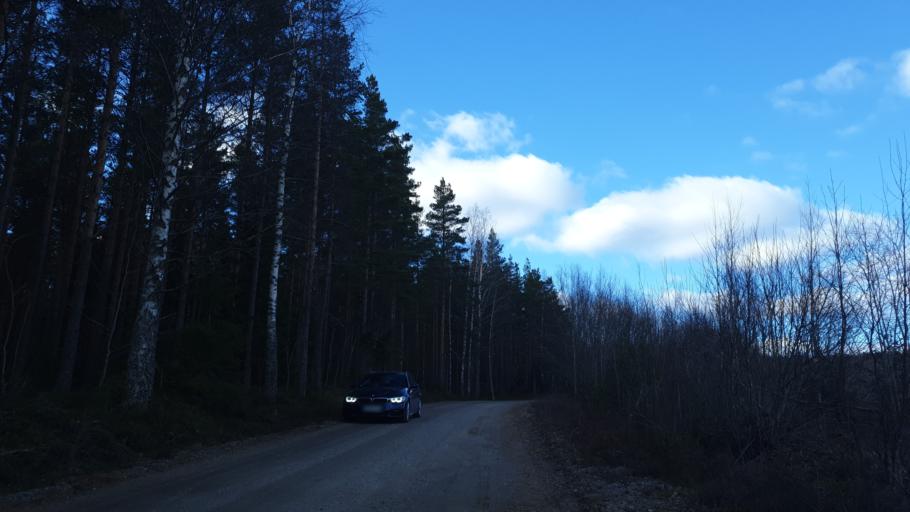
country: SE
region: OErebro
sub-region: Orebro Kommun
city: Garphyttan
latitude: 59.3568
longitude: 14.9781
